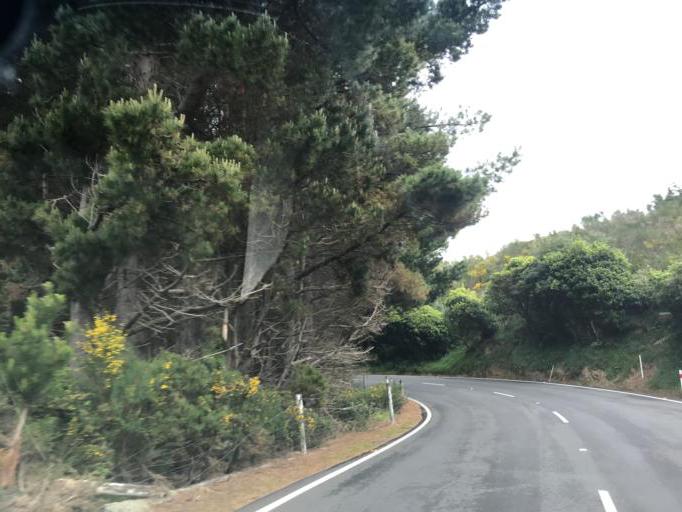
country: NZ
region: Wellington
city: Petone
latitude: -41.2119
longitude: 174.7958
